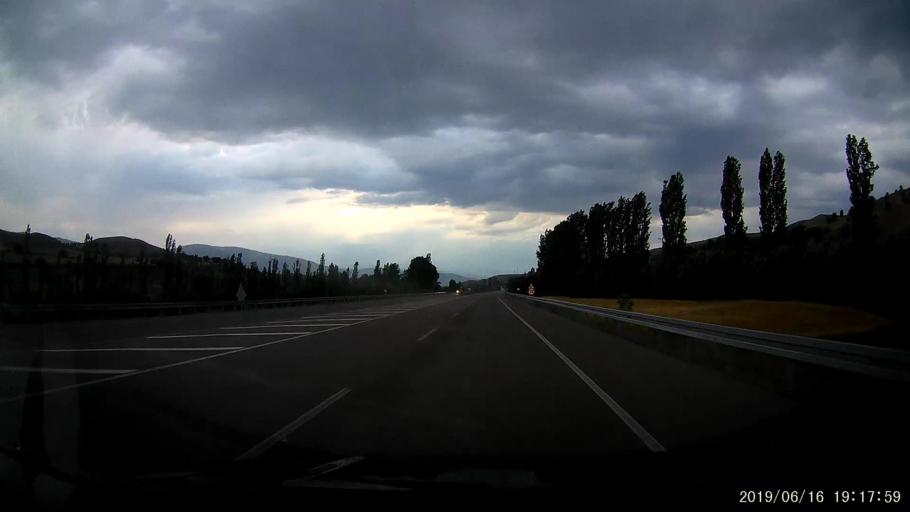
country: TR
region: Sivas
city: Akincilar
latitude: 40.0943
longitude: 38.4705
